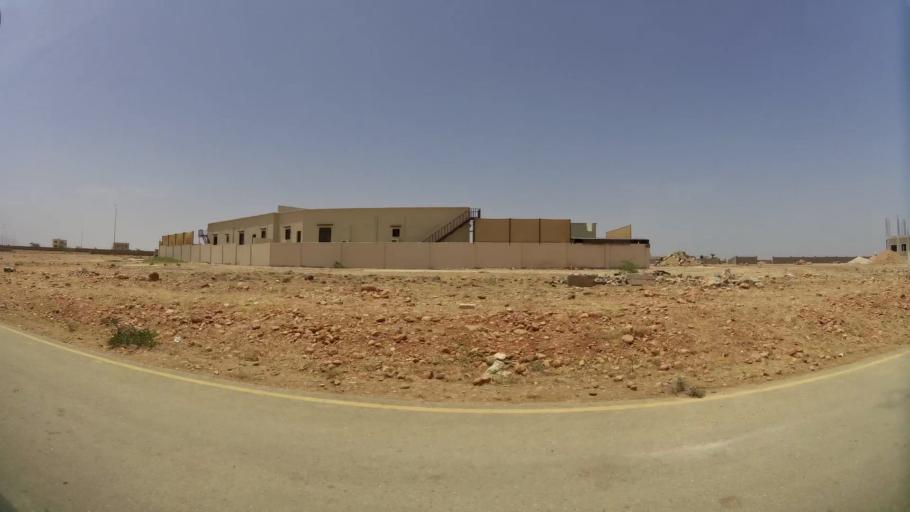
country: OM
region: Zufar
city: Salalah
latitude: 17.0902
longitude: 54.1840
